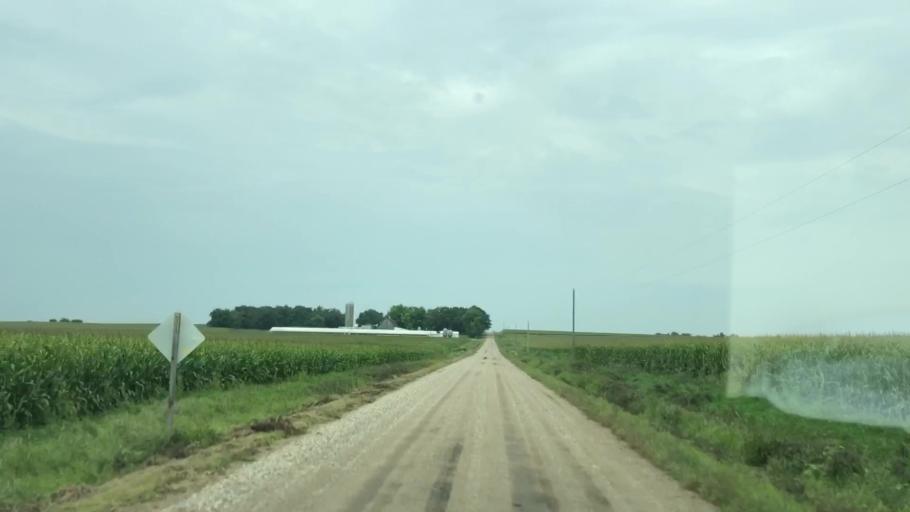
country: US
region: Iowa
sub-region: O'Brien County
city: Sheldon
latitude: 43.1874
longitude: -95.9018
